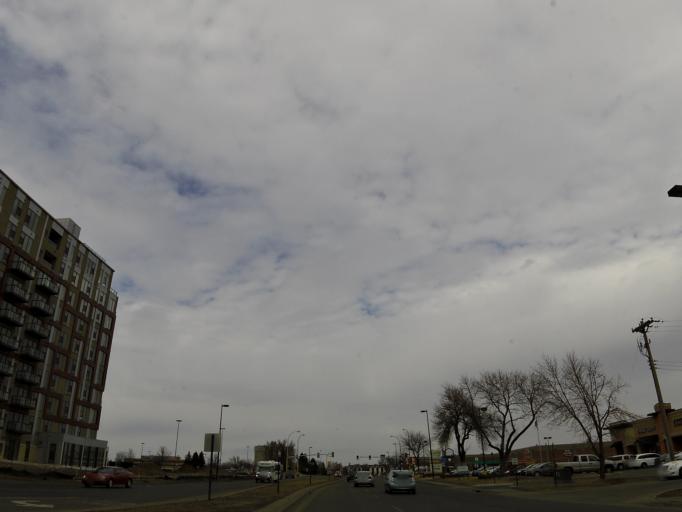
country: US
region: Minnesota
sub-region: Hennepin County
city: Edina
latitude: 44.8786
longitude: -93.3212
